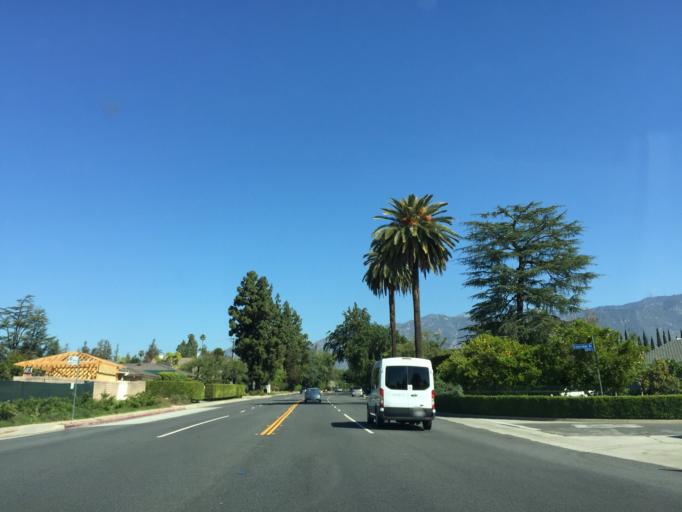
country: US
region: California
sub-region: Los Angeles County
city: East Pasadena
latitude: 34.1317
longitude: -118.0932
